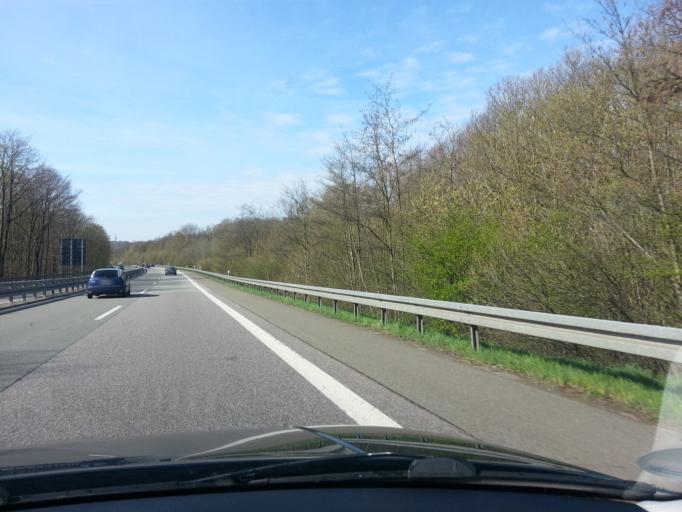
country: DE
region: Saarland
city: Sulzbach
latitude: 49.2894
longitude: 7.0231
